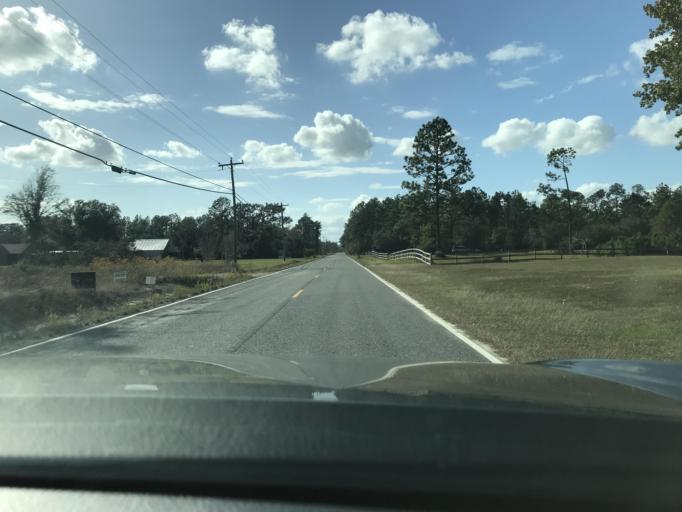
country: US
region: Louisiana
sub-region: Calcasieu Parish
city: Moss Bluff
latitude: 30.3226
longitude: -93.2661
